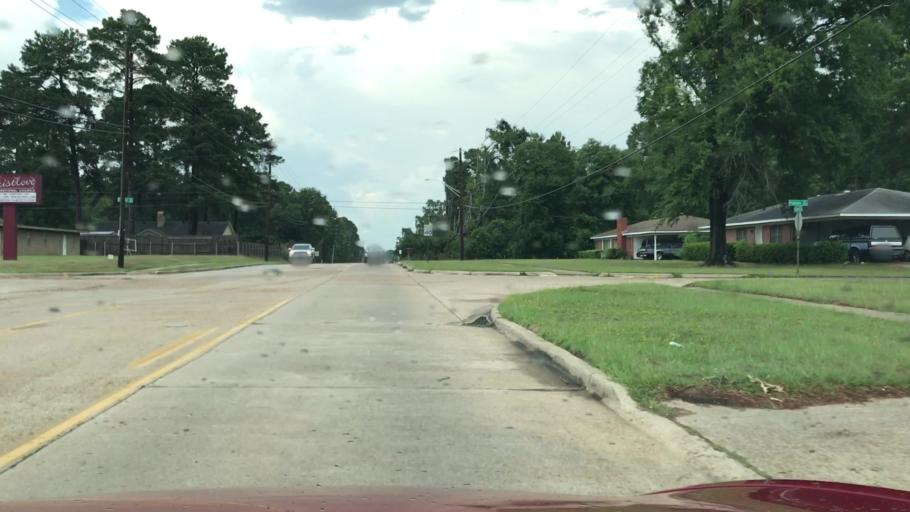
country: US
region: Louisiana
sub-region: De Soto Parish
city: Stonewall
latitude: 32.3938
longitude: -93.7804
